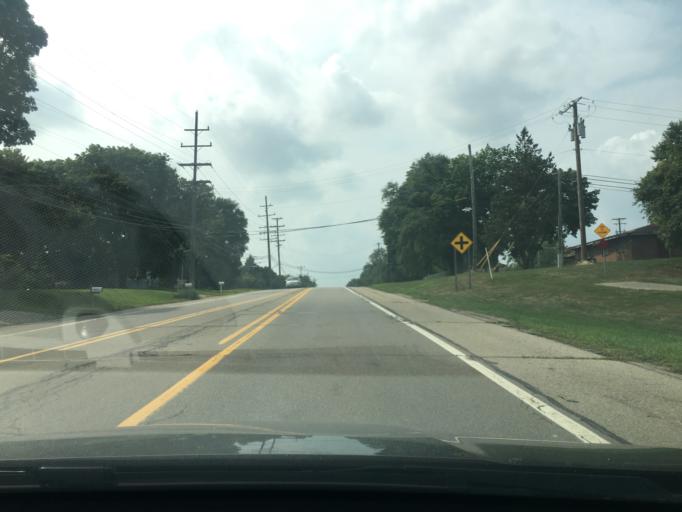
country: US
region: Michigan
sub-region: Oakland County
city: Rochester Hills
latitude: 42.6345
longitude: -83.1945
